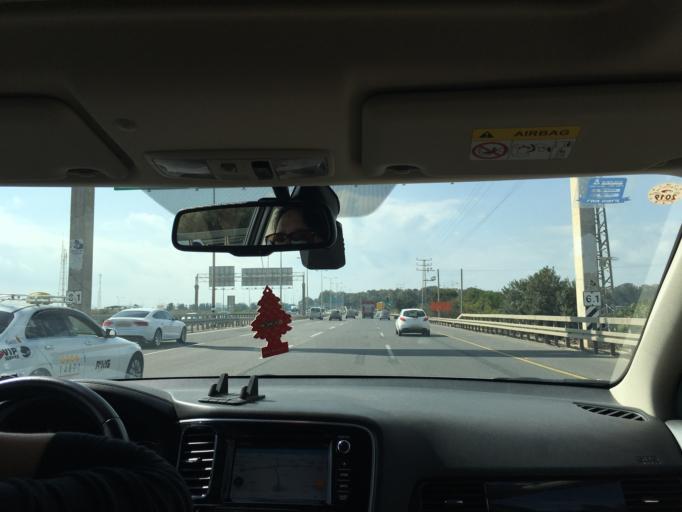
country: IL
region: Tel Aviv
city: Ramat HaSharon
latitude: 32.1381
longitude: 34.8232
